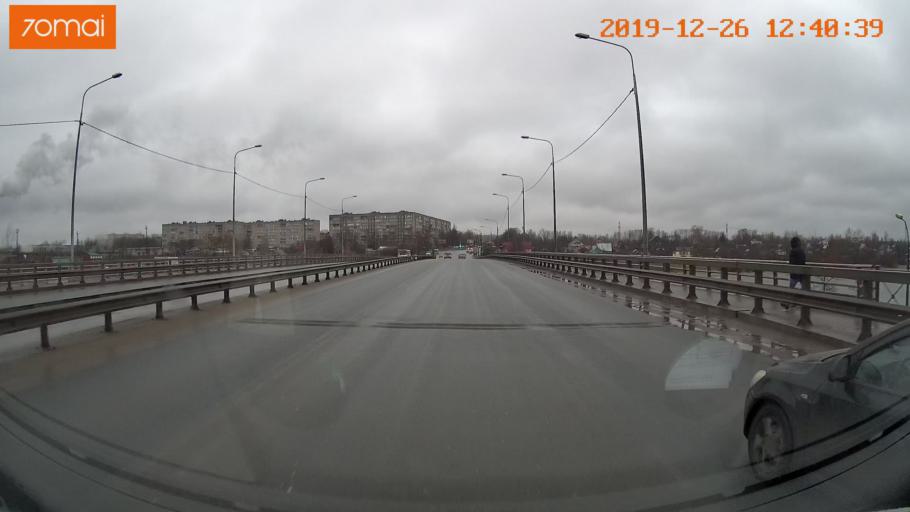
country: RU
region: Vologda
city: Tonshalovo
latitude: 59.1430
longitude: 37.9700
